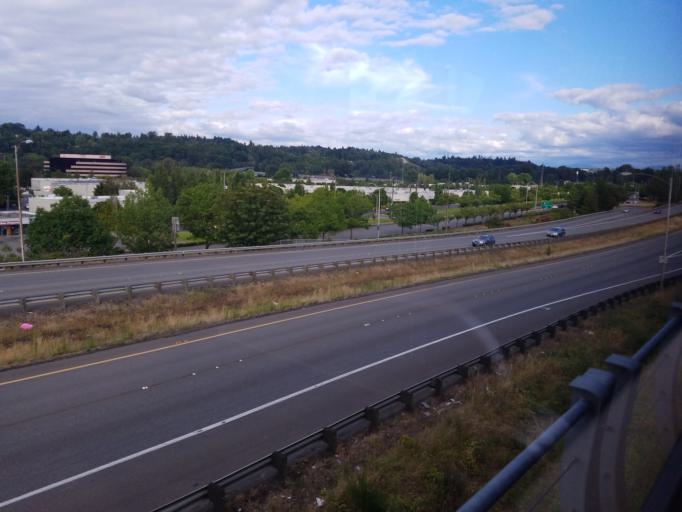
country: US
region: Washington
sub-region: King County
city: Riverton
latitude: 47.4880
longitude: -122.2796
